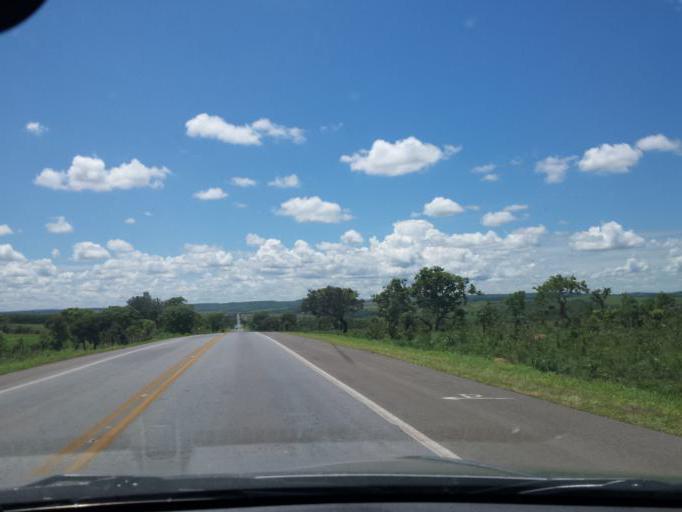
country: BR
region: Goias
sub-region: Cristalina
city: Cristalina
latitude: -16.5704
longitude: -47.7898
